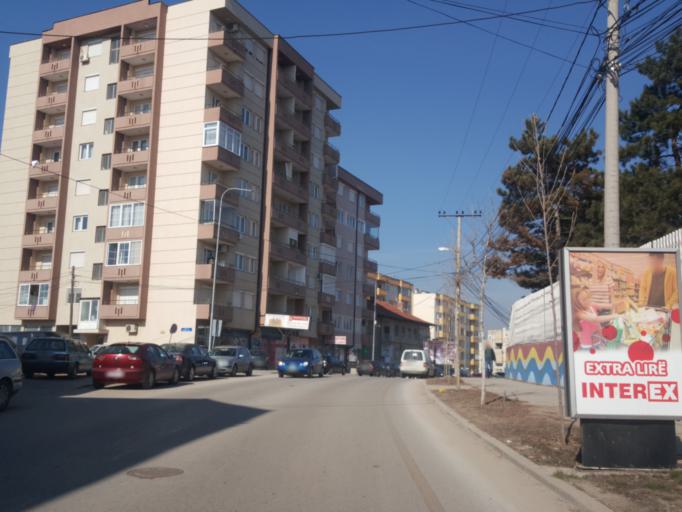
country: XK
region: Mitrovica
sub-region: Vushtrri
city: Vushtrri
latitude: 42.8243
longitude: 20.9634
